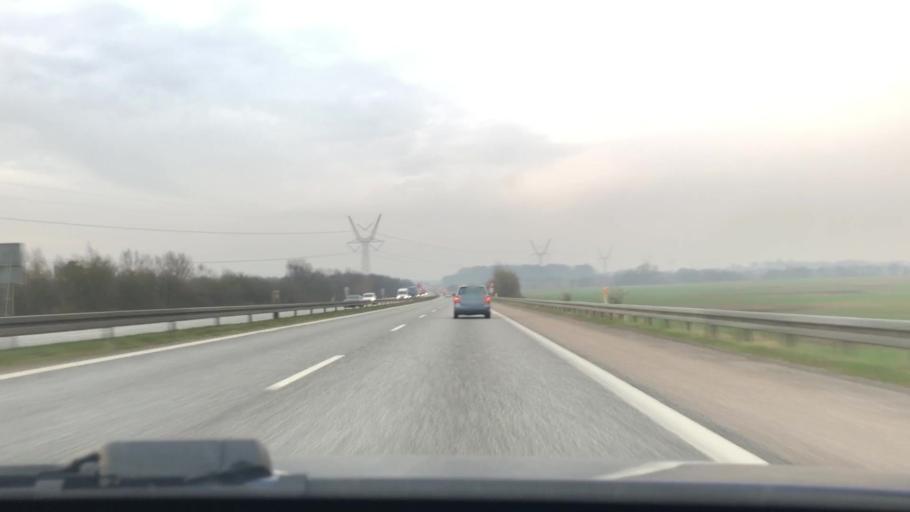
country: DK
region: South Denmark
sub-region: Kolding Kommune
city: Christiansfeld
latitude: 55.3509
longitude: 9.4456
